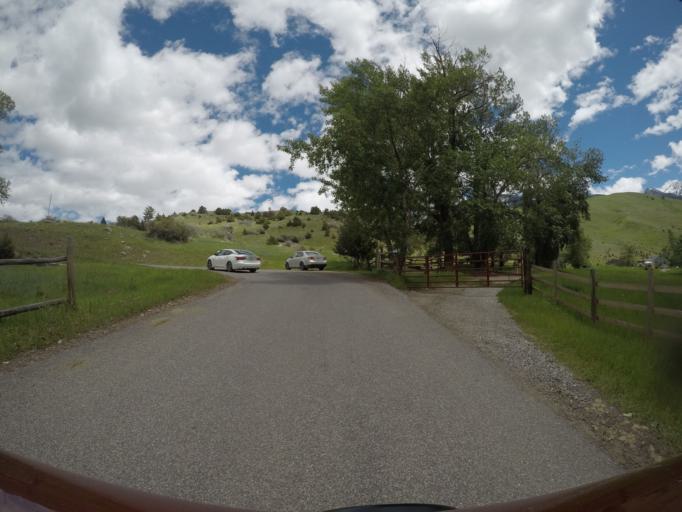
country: US
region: Montana
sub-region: Park County
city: Livingston
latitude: 45.4967
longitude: -110.5604
